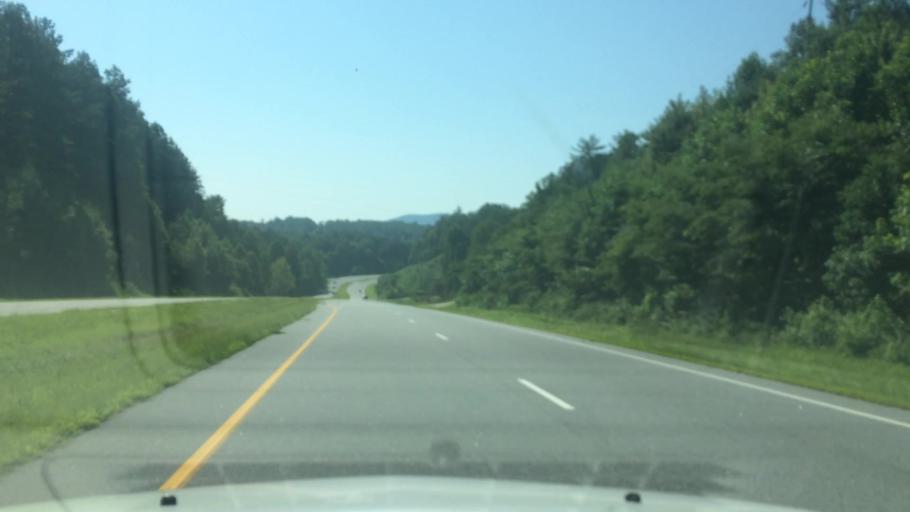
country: US
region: North Carolina
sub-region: Caldwell County
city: Lenoir
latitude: 35.9532
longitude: -81.5551
